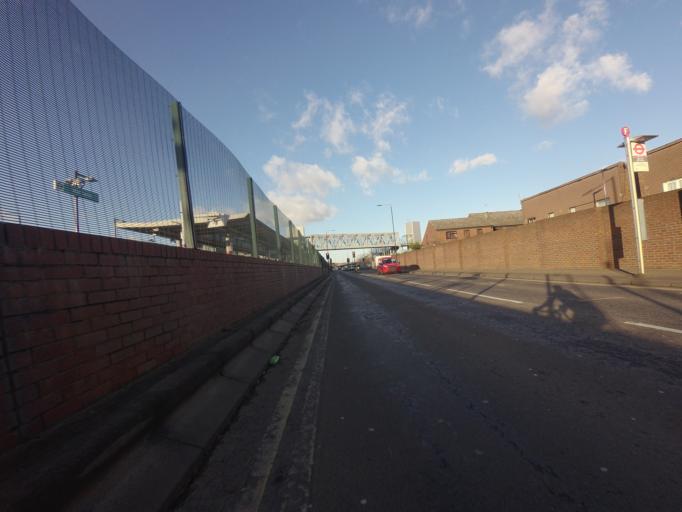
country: GB
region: England
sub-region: Greater London
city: Poplar
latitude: 51.5202
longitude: 0.0045
